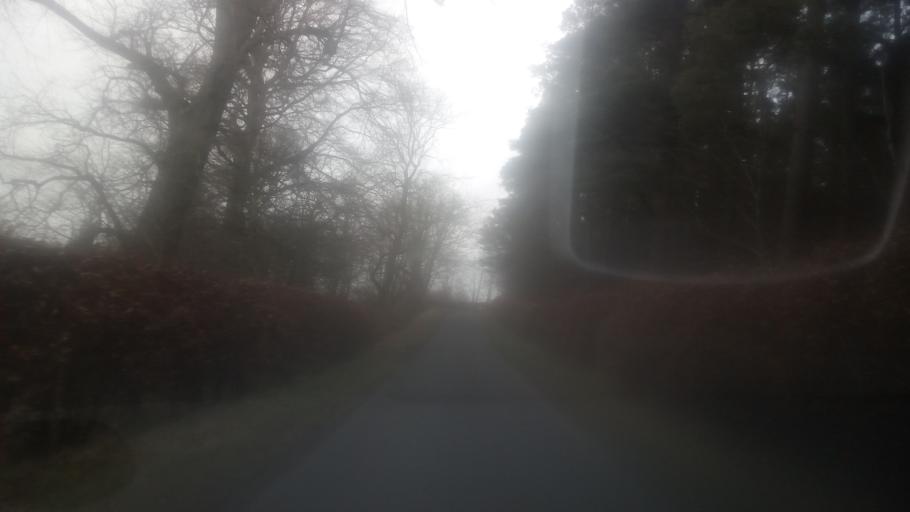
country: GB
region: Scotland
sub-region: The Scottish Borders
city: Jedburgh
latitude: 55.4800
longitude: -2.5253
